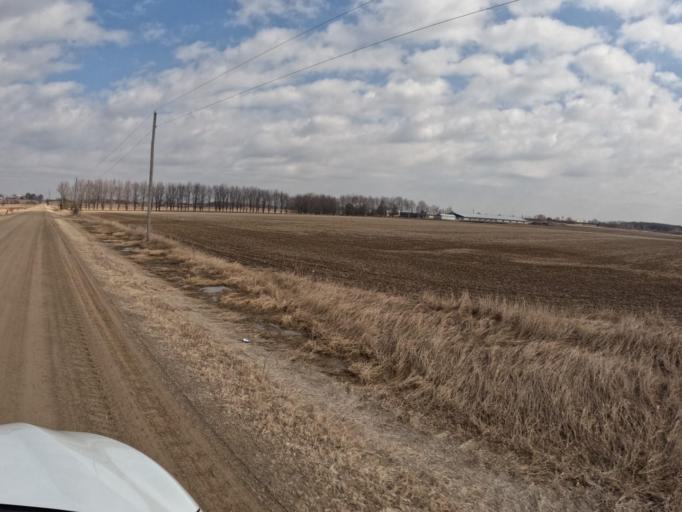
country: CA
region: Ontario
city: Orangeville
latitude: 43.9236
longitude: -80.2401
